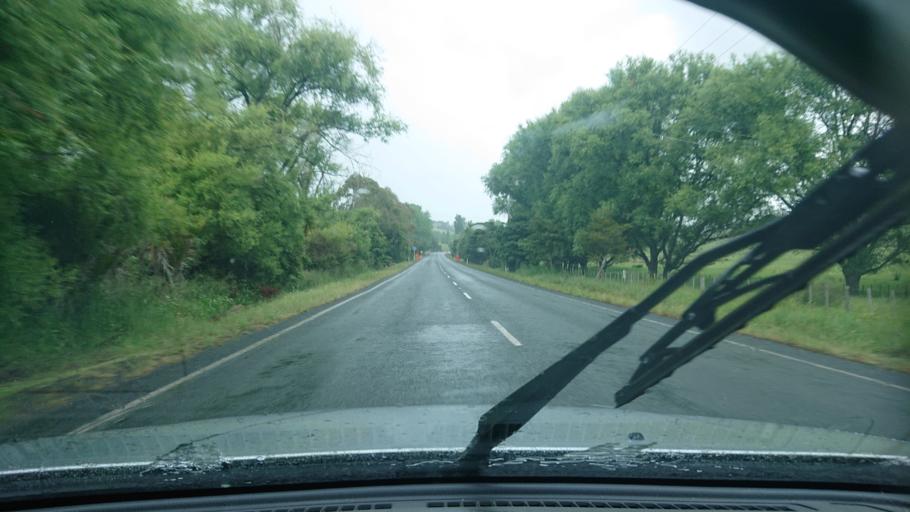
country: NZ
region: Auckland
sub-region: Auckland
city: Wellsford
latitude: -36.3170
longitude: 174.4917
